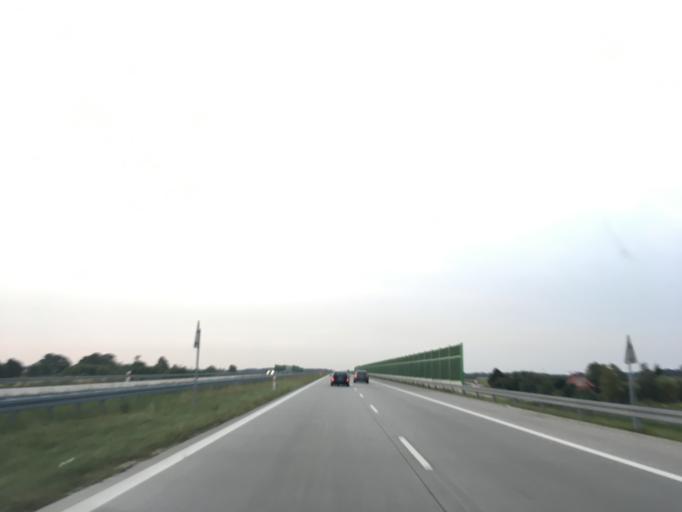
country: PL
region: Lodz Voivodeship
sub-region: Powiat lodzki wschodni
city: Tuszyn
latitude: 51.5826
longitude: 19.5919
